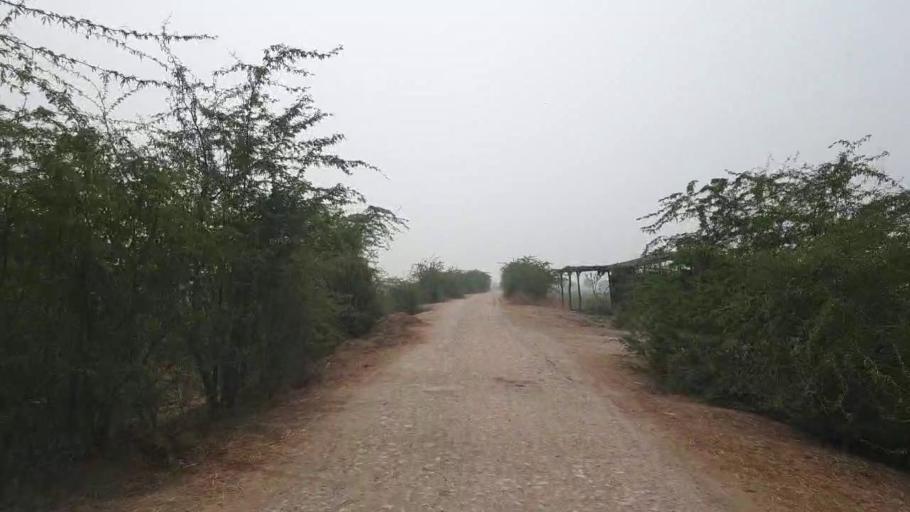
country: PK
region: Sindh
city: Kario
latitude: 24.6511
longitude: 68.6408
